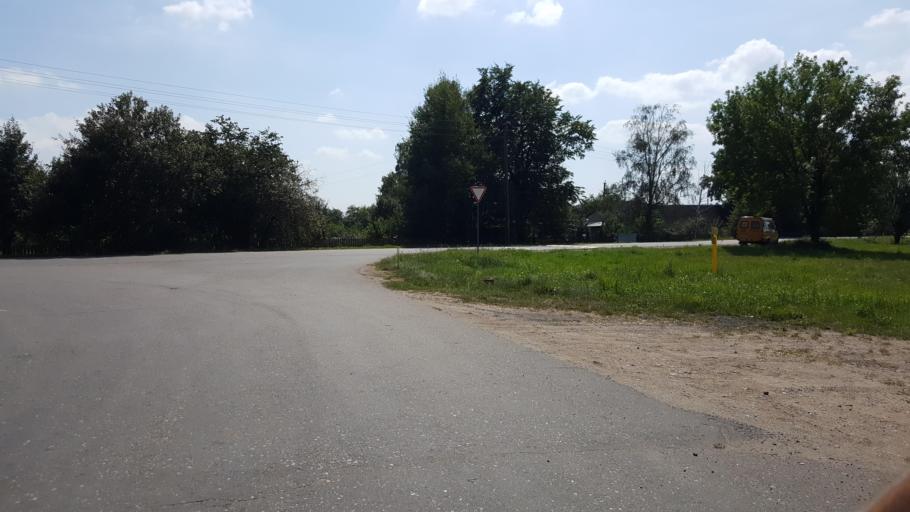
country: PL
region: Podlasie
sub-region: Powiat hajnowski
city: Czeremcha
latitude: 52.4950
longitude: 23.5600
